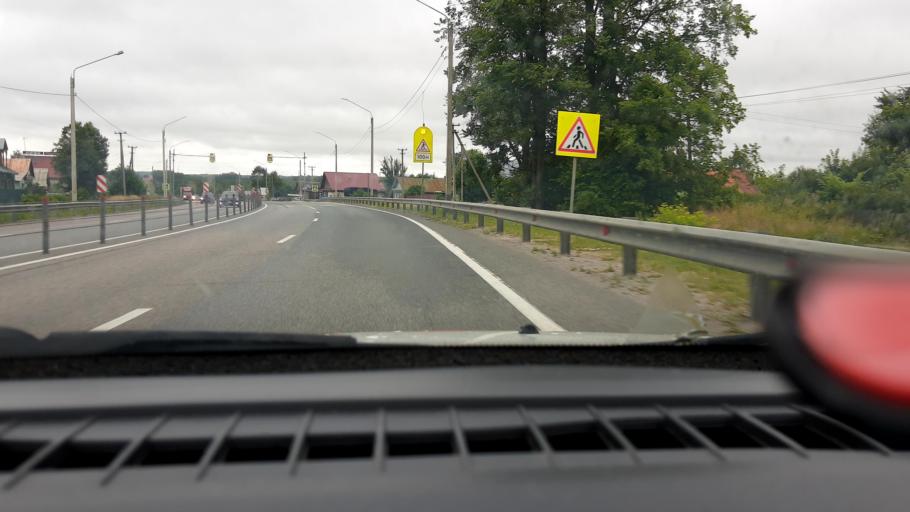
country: RU
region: Vladimir
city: Novovyazniki
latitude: 56.1731
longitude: 42.4187
